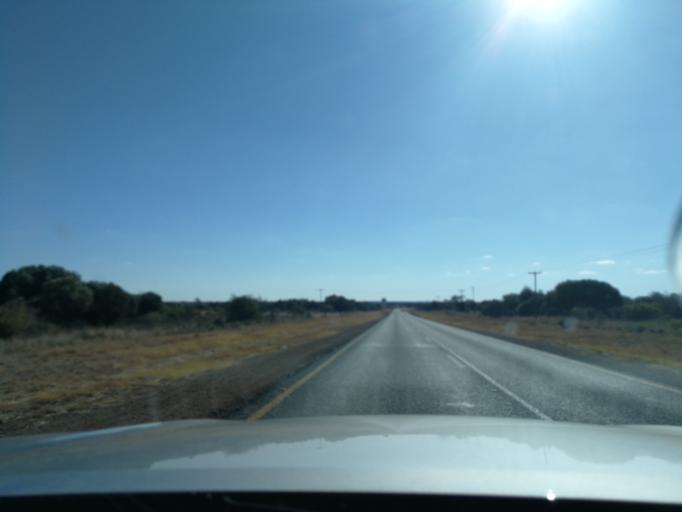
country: ZA
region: North-West
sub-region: Ngaka Modiri Molema District Municipality
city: Zeerust
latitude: -25.7616
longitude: 25.9736
